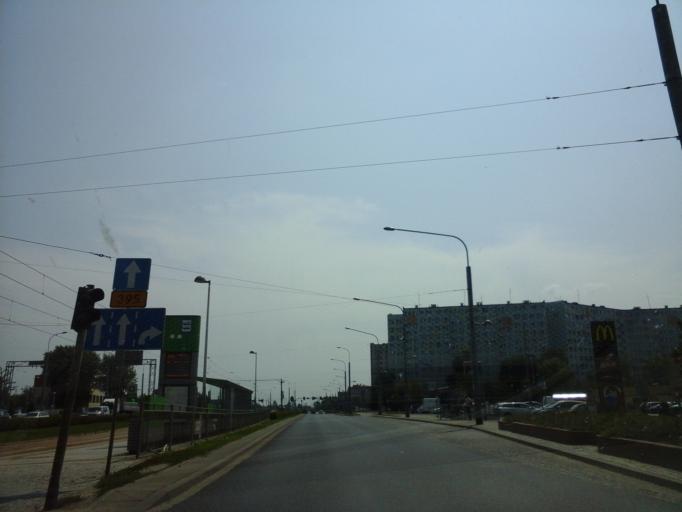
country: PL
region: Lower Silesian Voivodeship
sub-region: Powiat wroclawski
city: Wroclaw
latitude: 51.0826
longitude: 17.0493
